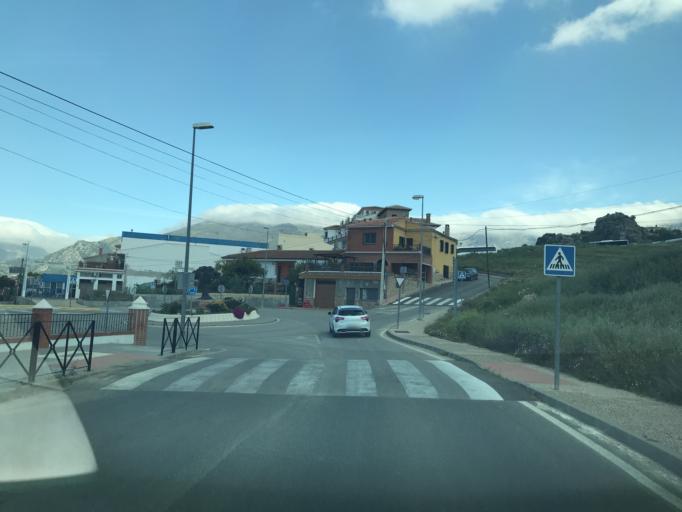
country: ES
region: Andalusia
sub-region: Provincia de Malaga
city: Periana
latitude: 36.9316
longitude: -4.1934
